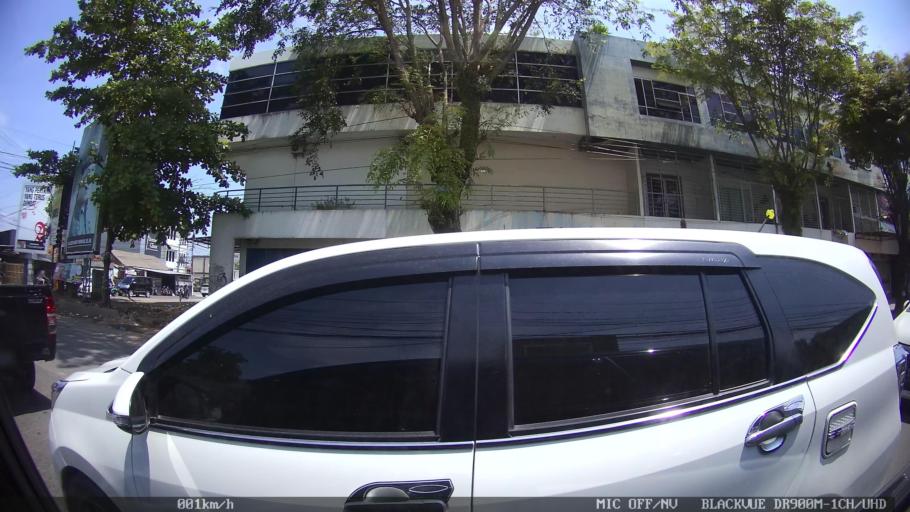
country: ID
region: Lampung
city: Kedaton
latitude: -5.3916
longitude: 105.2810
